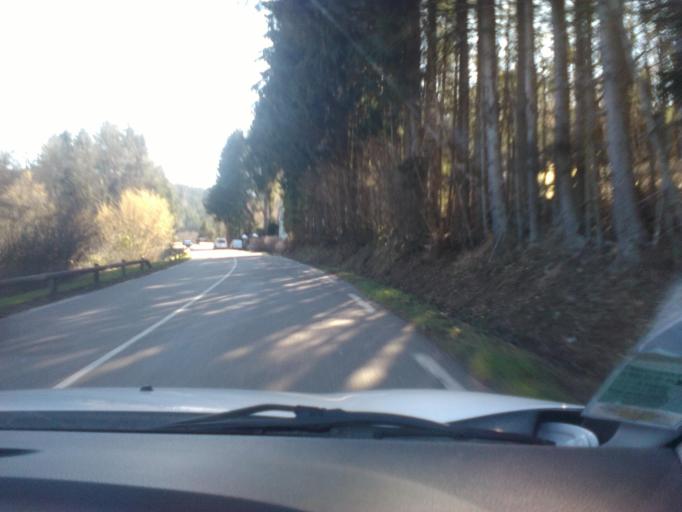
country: FR
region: Alsace
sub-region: Departement du Haut-Rhin
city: Sainte-Marie-aux-Mines
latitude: 48.3540
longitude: 7.1315
